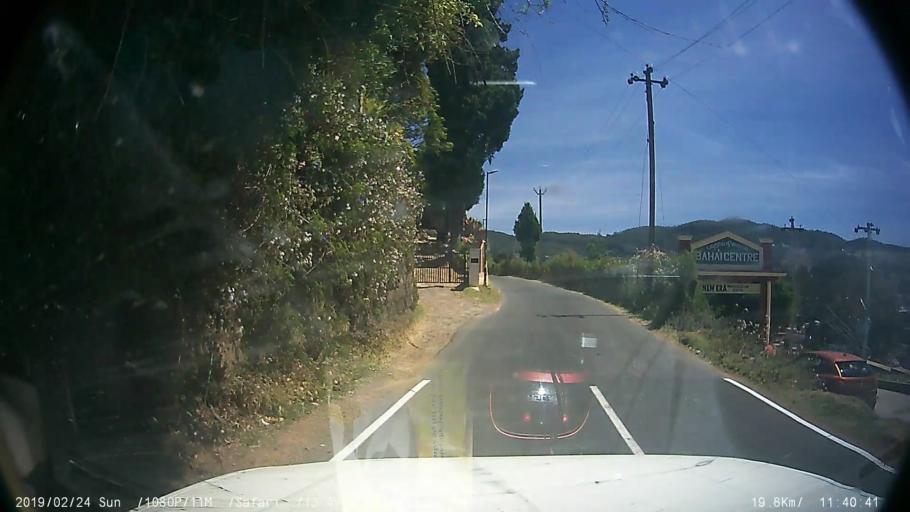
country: IN
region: Tamil Nadu
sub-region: Nilgiri
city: Ooty
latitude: 11.4157
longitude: 76.7034
